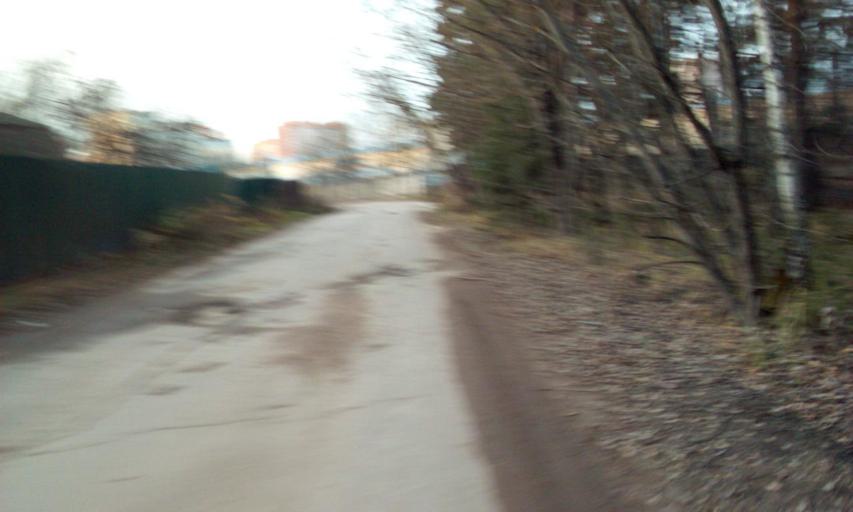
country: RU
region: Moskovskaya
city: Krasnoznamensk
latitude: 55.5799
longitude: 37.0446
